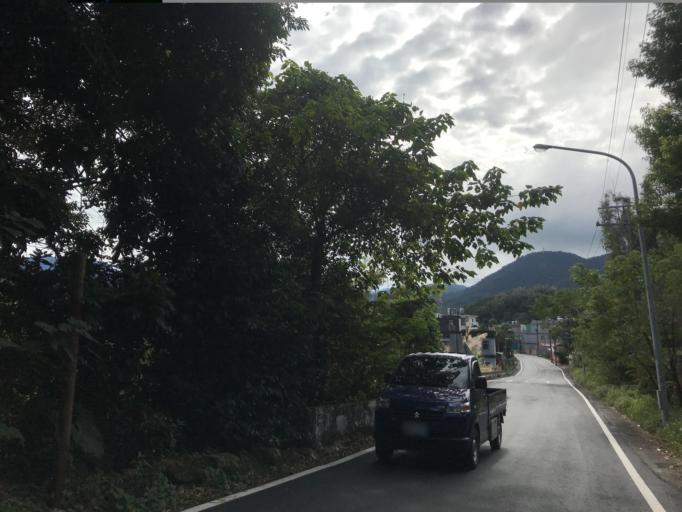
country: TW
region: Taiwan
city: Daxi
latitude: 24.8342
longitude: 121.2447
